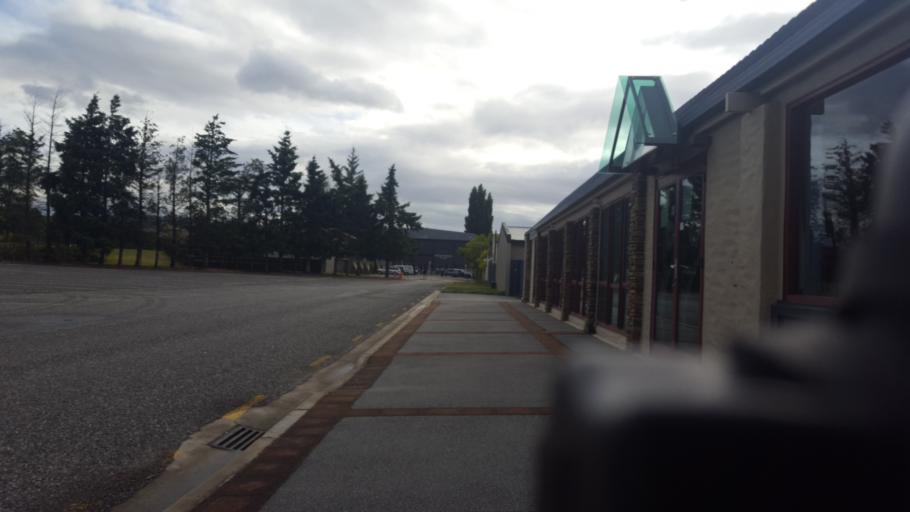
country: NZ
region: Otago
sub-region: Queenstown-Lakes District
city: Wanaka
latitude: -45.2450
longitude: 169.3826
